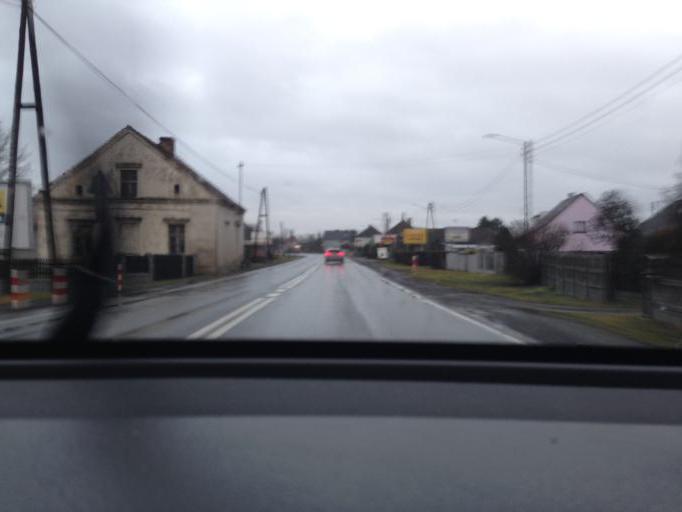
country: PL
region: Opole Voivodeship
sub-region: Powiat opolski
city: Wegry
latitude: 50.7114
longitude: 17.9896
